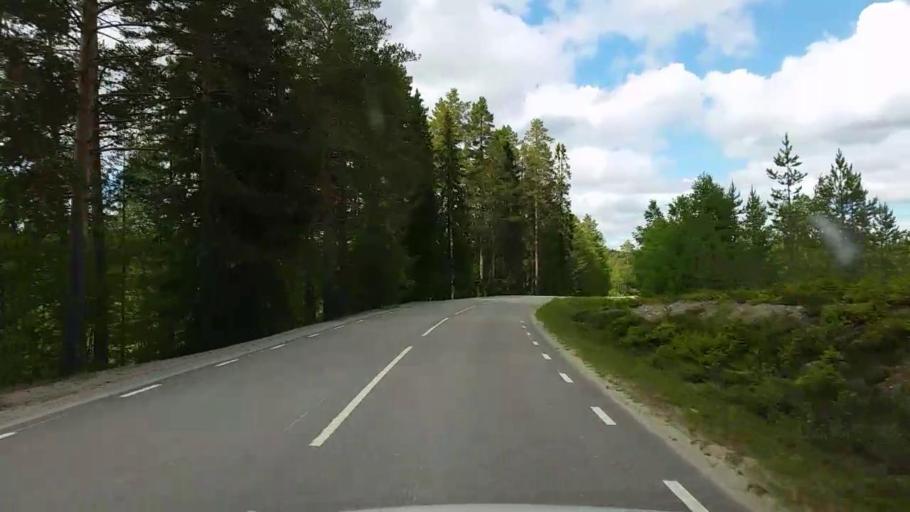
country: SE
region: Gaevleborg
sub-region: Bollnas Kommun
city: Vittsjo
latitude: 61.1476
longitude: 16.1625
